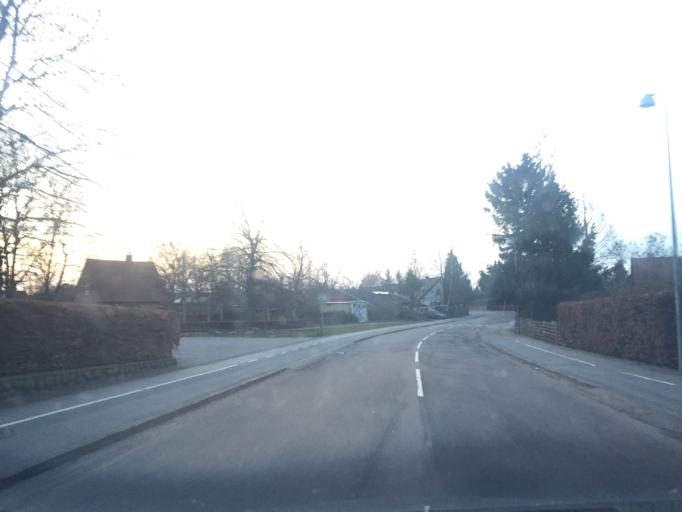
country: DK
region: Capital Region
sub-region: Hoje-Taastrup Kommune
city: Taastrup
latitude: 55.6436
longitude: 12.3082
